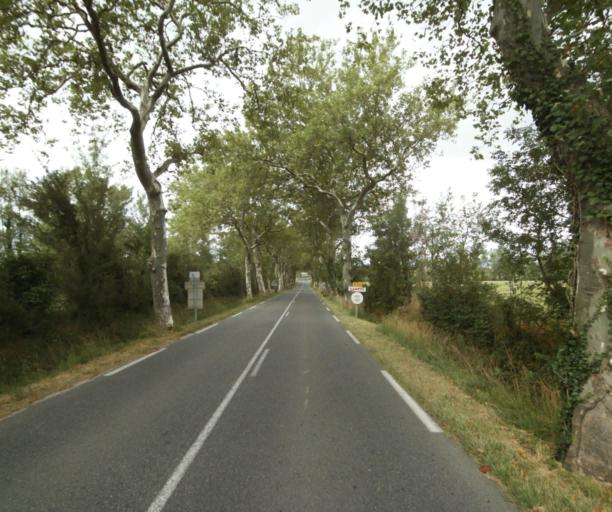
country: FR
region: Midi-Pyrenees
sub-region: Departement du Tarn
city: Soreze
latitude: 43.4584
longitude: 2.0777
